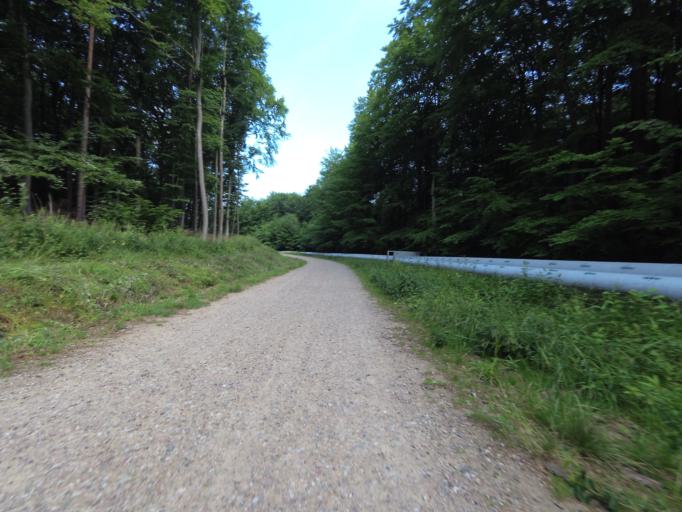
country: PL
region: Pomeranian Voivodeship
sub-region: Gdynia
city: Wielki Kack
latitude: 54.4797
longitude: 18.5010
